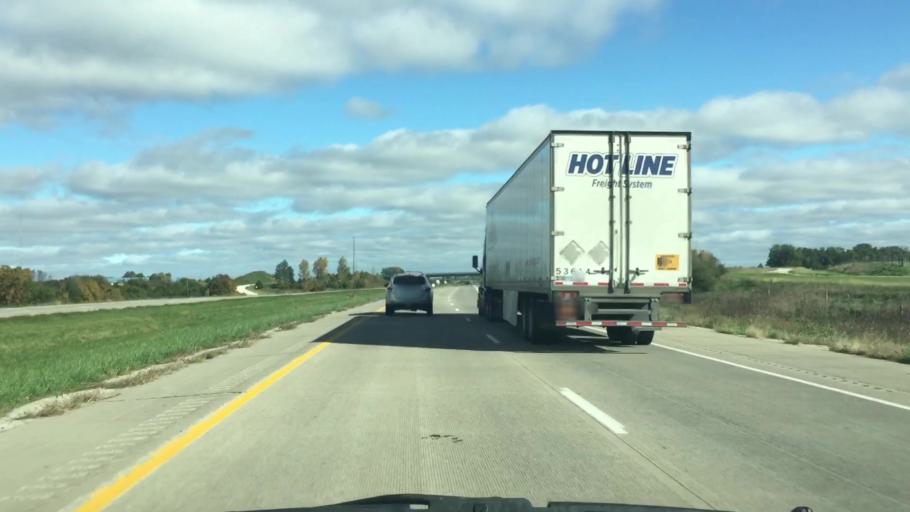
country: US
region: Iowa
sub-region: Decatur County
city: Leon
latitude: 40.7970
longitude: -93.8337
